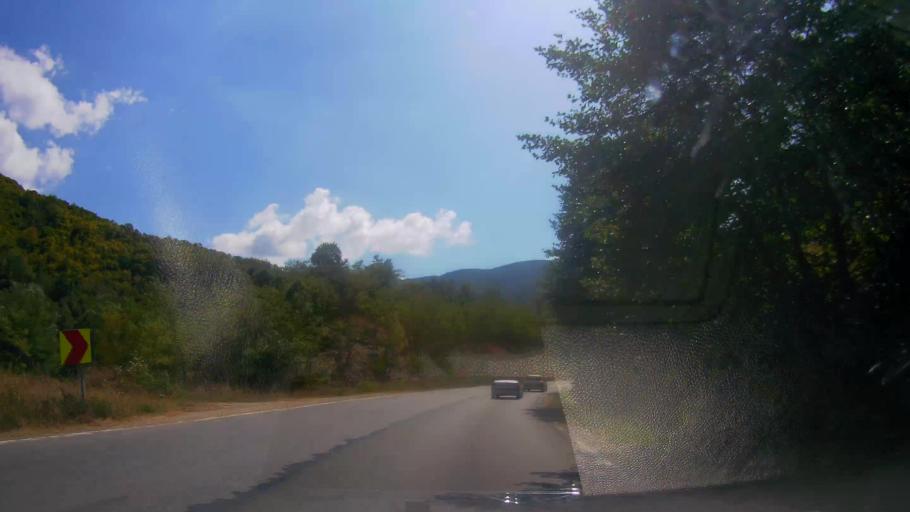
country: BG
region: Stara Zagora
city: Gurkovo
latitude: 42.7144
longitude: 25.7184
